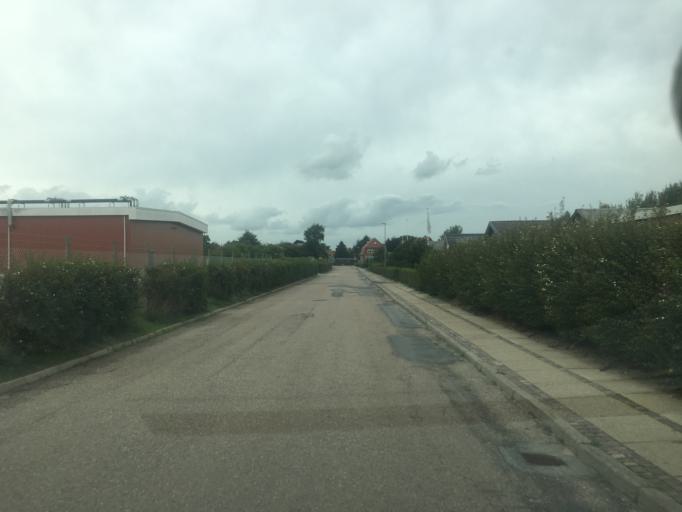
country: DK
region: South Denmark
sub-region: Tonder Kommune
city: Tonder
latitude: 54.9294
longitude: 8.8573
